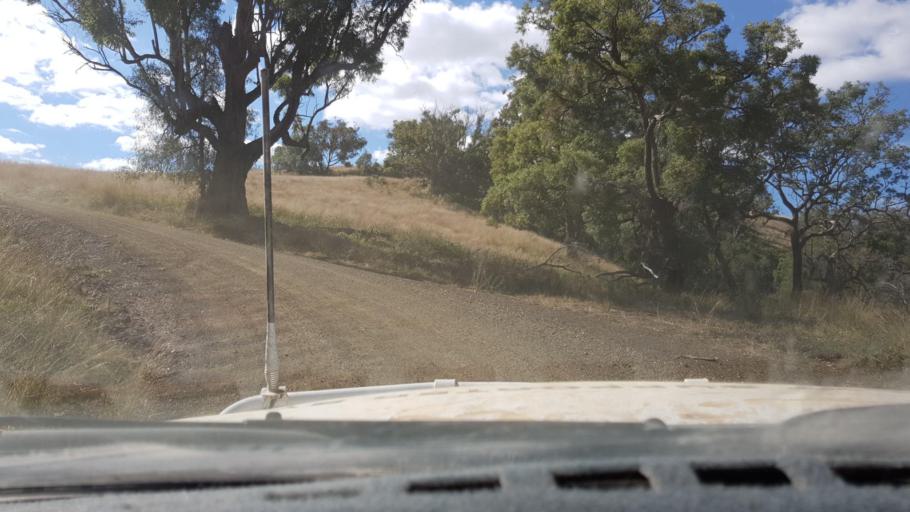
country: AU
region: New South Wales
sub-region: Tamworth Municipality
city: Manilla
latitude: -30.4486
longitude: 150.7814
